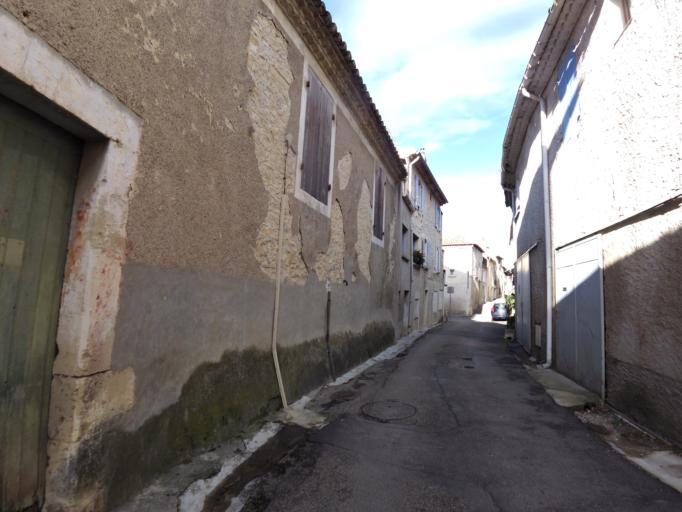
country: FR
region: Languedoc-Roussillon
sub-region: Departement du Gard
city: Langlade
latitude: 43.8029
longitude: 4.2482
